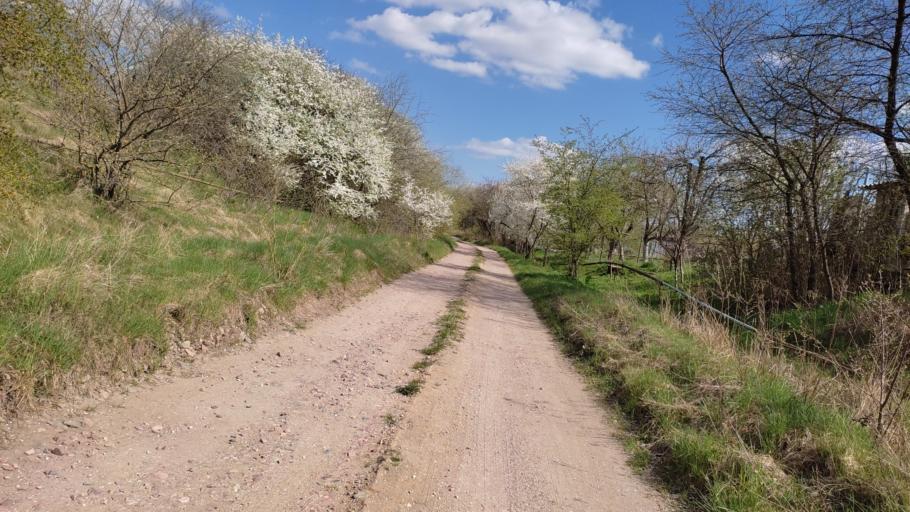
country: BY
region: Grodnenskaya
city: Hrodna
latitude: 53.6570
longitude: 23.8984
